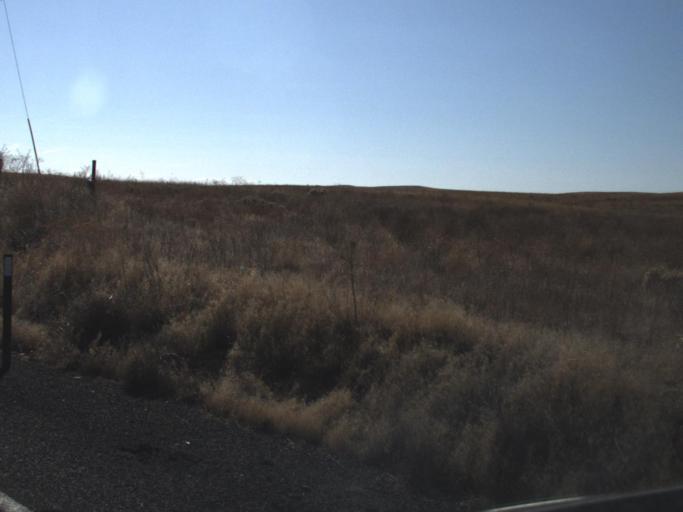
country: US
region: Washington
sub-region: Franklin County
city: Connell
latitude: 46.7144
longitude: -118.5480
